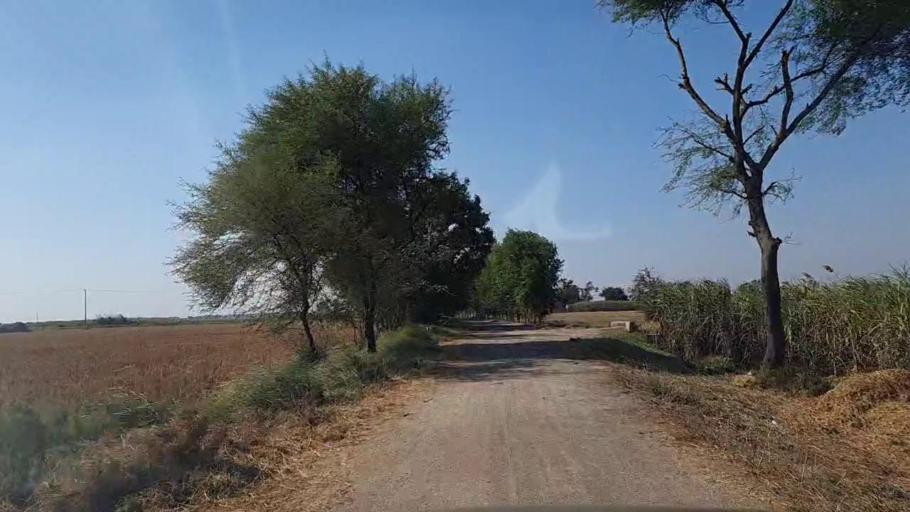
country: PK
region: Sindh
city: Mirpur Batoro
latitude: 24.7157
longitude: 68.2347
